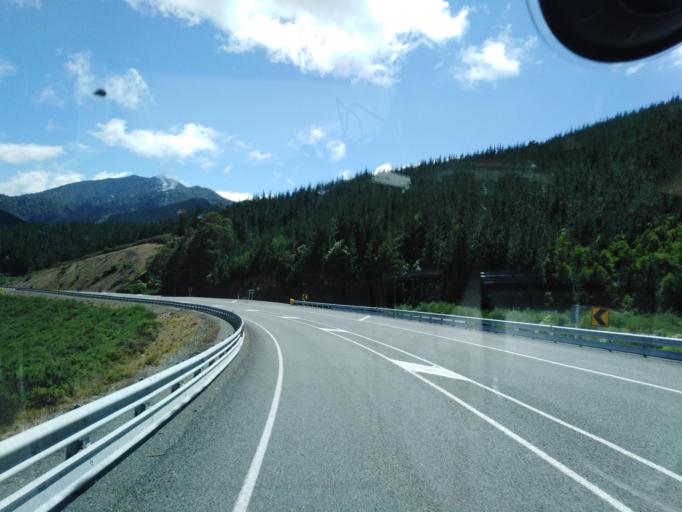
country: NZ
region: Nelson
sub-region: Nelson City
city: Nelson
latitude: -41.1850
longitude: 173.5596
